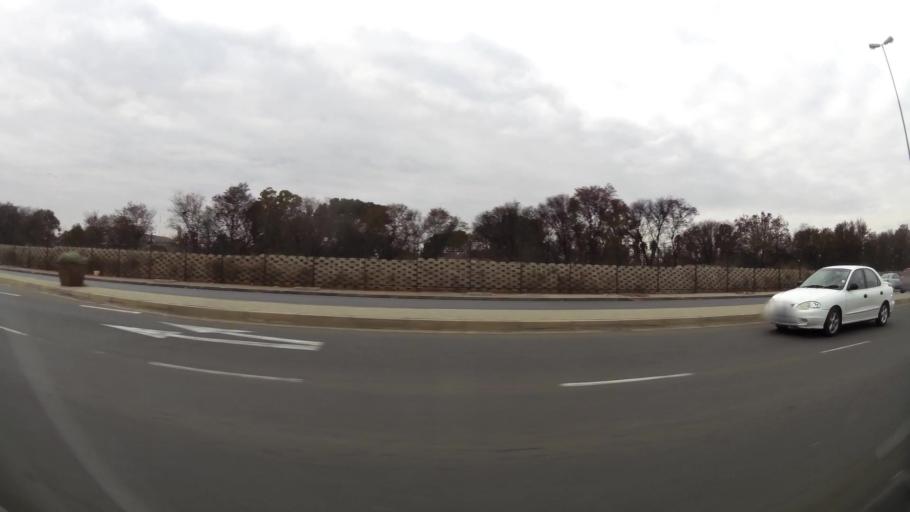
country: ZA
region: Orange Free State
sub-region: Mangaung Metropolitan Municipality
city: Bloemfontein
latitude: -29.1127
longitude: 26.2014
